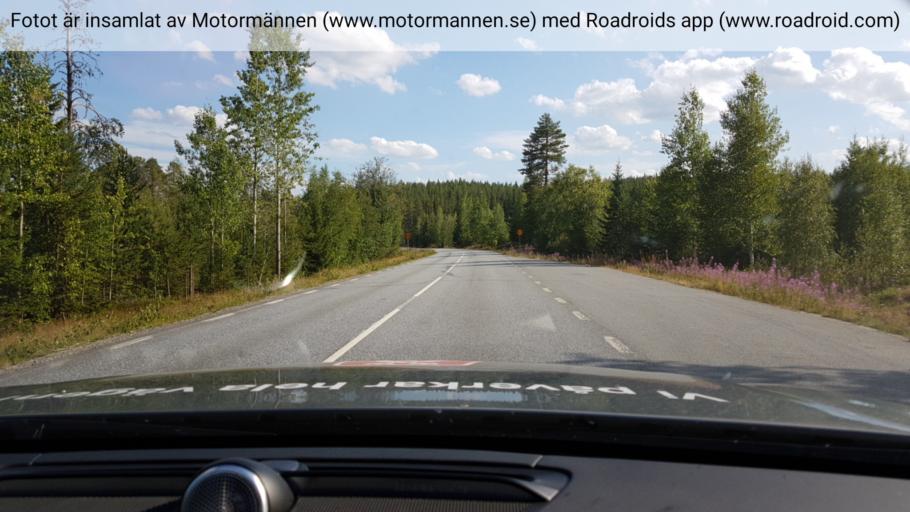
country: SE
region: Vaesterbotten
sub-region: Dorotea Kommun
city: Dorotea
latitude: 63.8981
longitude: 16.3604
